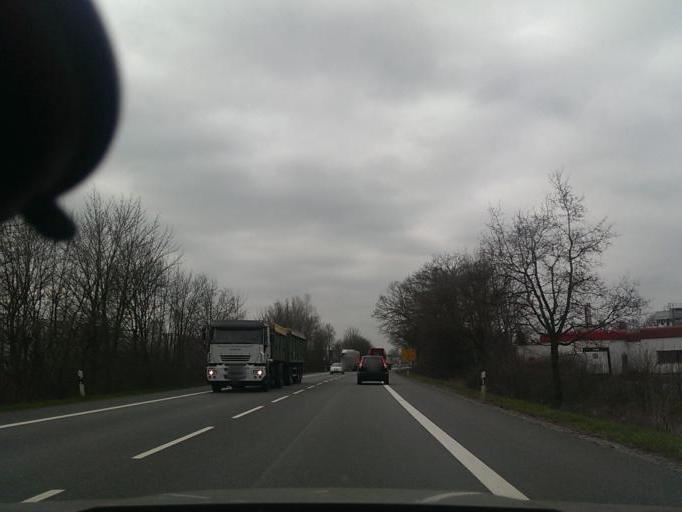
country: DE
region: North Rhine-Westphalia
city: Rietberg
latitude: 51.7912
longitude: 8.4254
